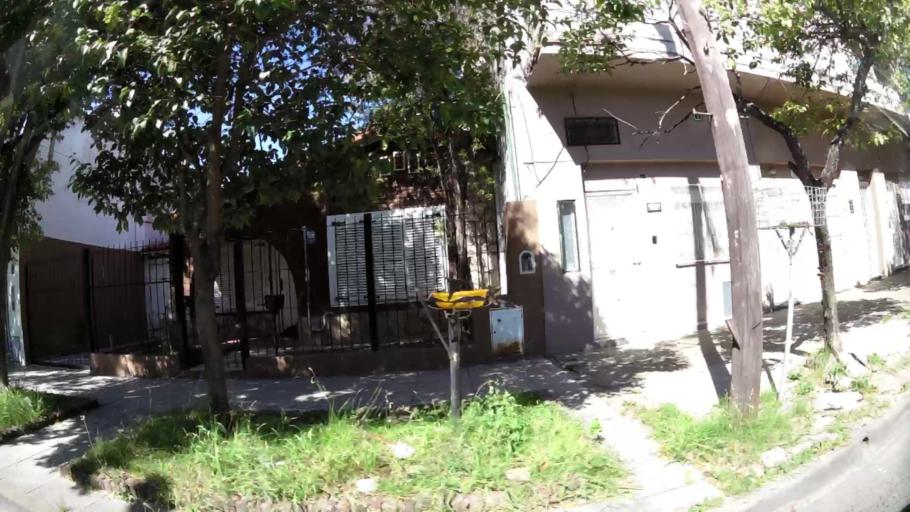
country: AR
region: Buenos Aires
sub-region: Partido de General San Martin
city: General San Martin
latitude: -34.5371
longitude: -58.5758
